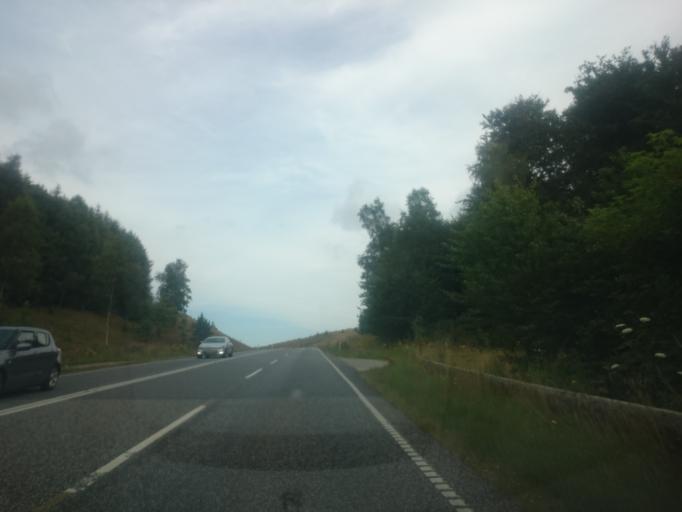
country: DK
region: South Denmark
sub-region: Vejle Kommune
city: Jelling
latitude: 55.6885
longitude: 9.3800
